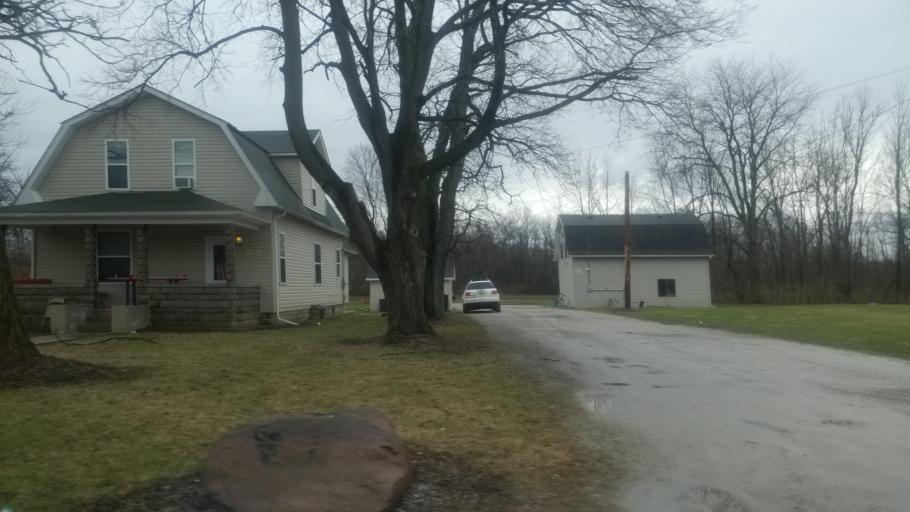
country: US
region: Ohio
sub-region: Wood County
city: Bowling Green
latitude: 41.3636
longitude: -83.6305
